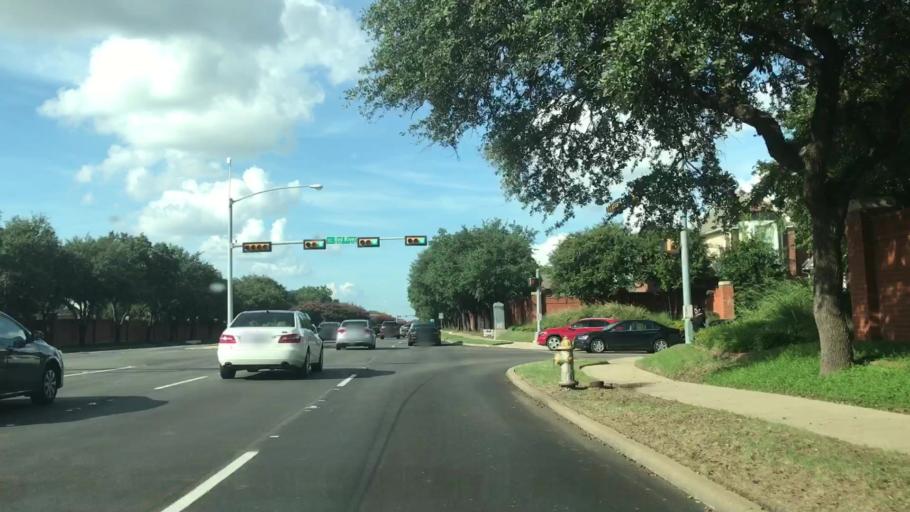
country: US
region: Texas
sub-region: Dallas County
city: Farmers Branch
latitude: 32.9298
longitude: -96.9520
